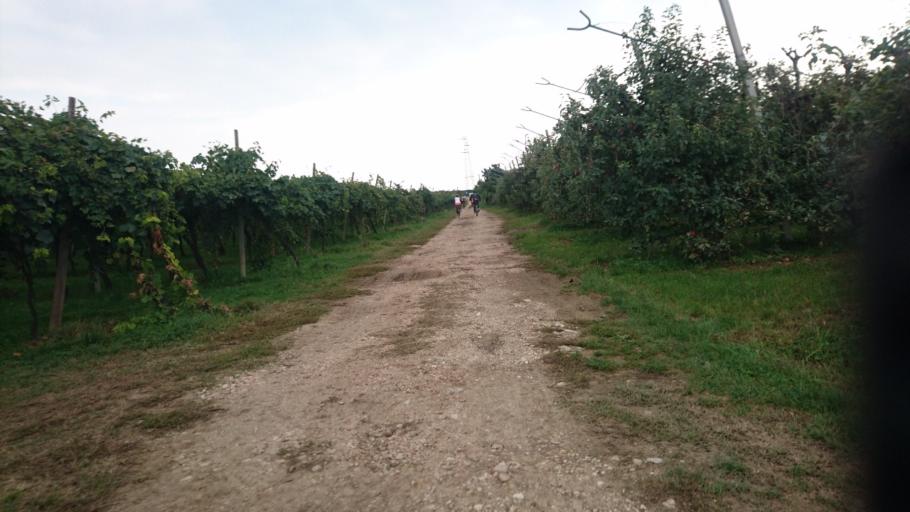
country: IT
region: Veneto
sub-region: Provincia di Verona
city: Caldierino-Rota
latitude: 45.4002
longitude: 11.1399
